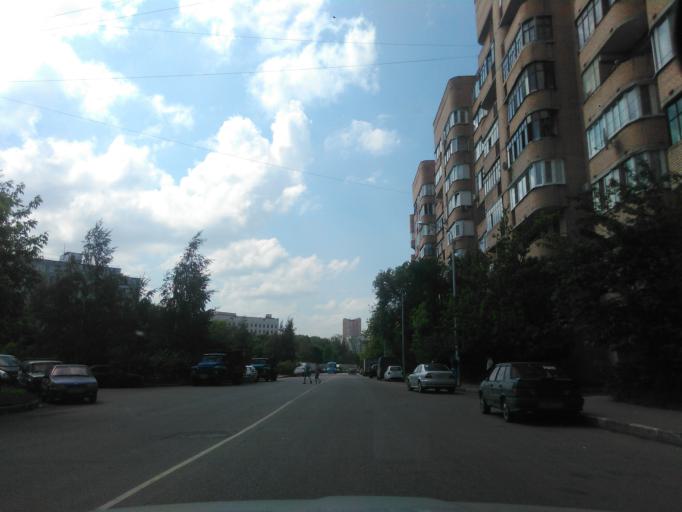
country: RU
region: Moscow
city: Vagonoremont
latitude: 55.8934
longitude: 37.5342
